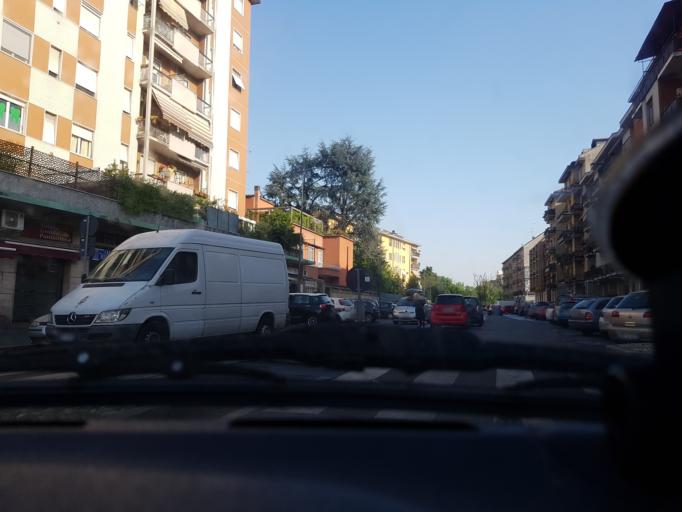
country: IT
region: Lombardy
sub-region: Citta metropolitana di Milano
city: Cesano Boscone
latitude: 45.4601
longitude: 9.0971
